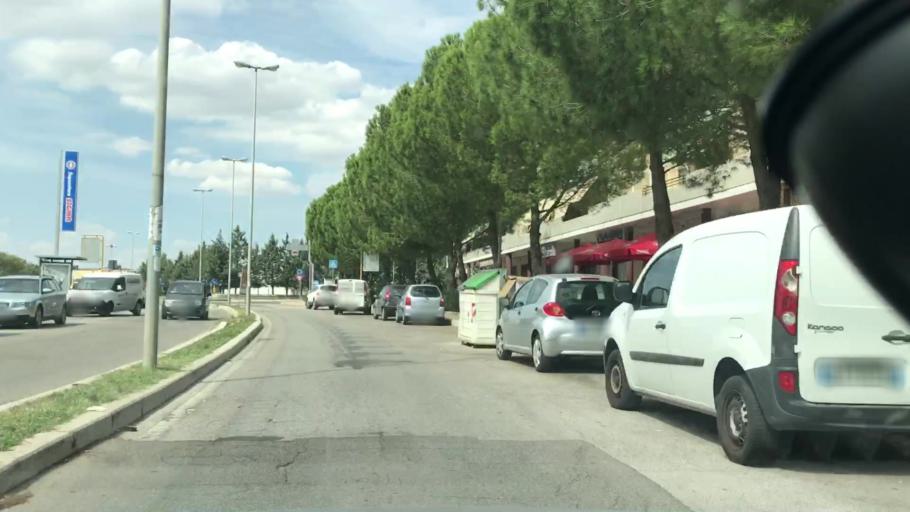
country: IT
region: Basilicate
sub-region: Provincia di Matera
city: Matera
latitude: 40.6784
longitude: 16.5813
